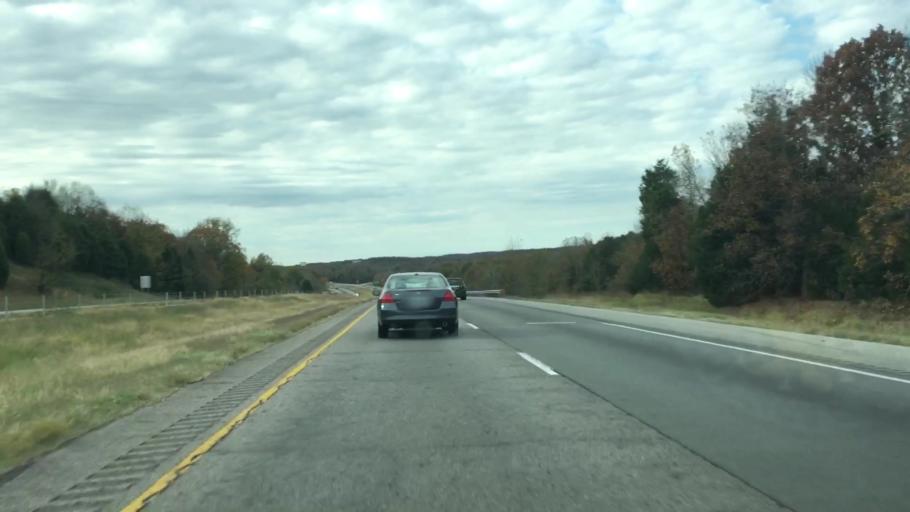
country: US
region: Arkansas
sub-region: Faulkner County
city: Conway
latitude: 35.1481
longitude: -92.5410
